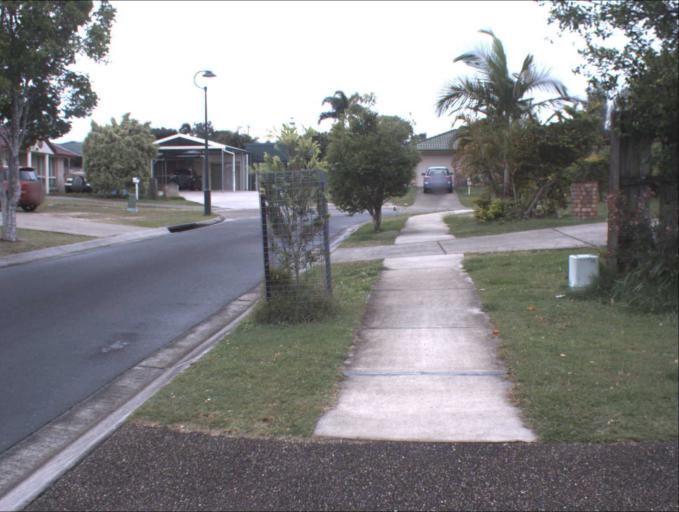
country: AU
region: Queensland
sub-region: Logan
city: Waterford West
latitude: -27.6863
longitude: 153.1144
